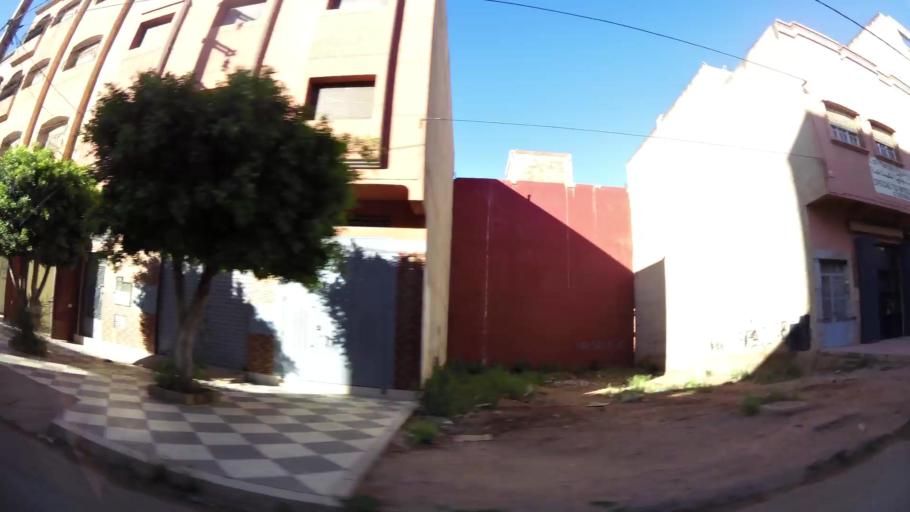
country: MA
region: Oriental
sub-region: Berkane-Taourirt
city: Berkane
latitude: 34.9313
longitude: -2.3422
